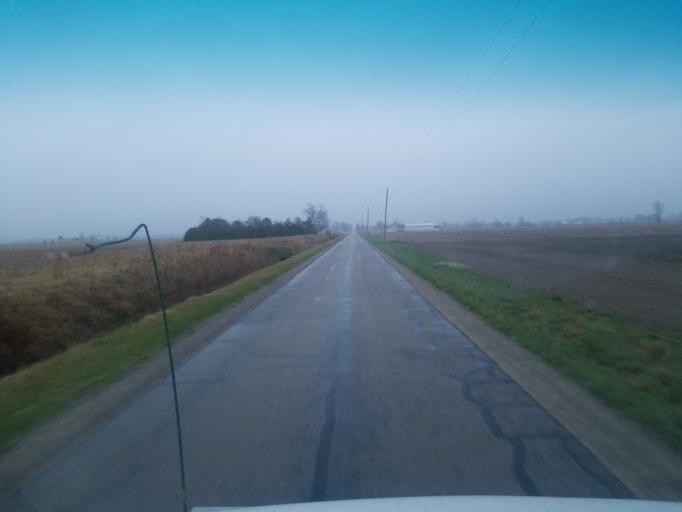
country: US
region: Ohio
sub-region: Henry County
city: Napoleon
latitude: 41.4133
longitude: -84.2194
